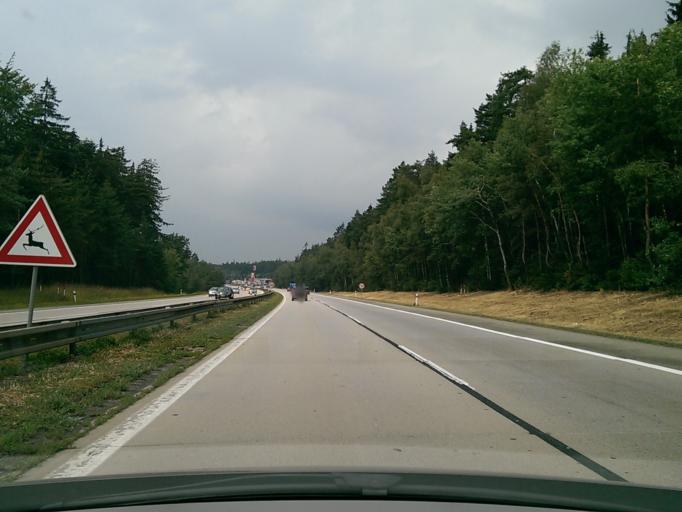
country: CZ
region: South Moravian
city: Zbraslav
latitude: 49.2685
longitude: 16.2877
